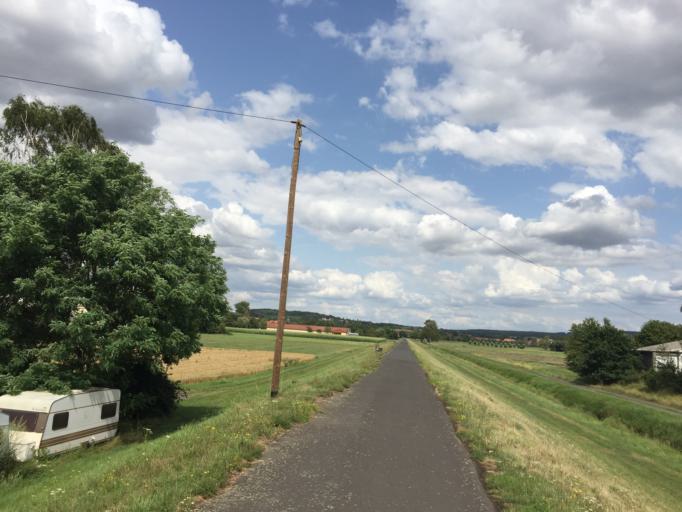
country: DE
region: Hesse
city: Schwalmstadt
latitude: 50.9058
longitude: 9.2387
